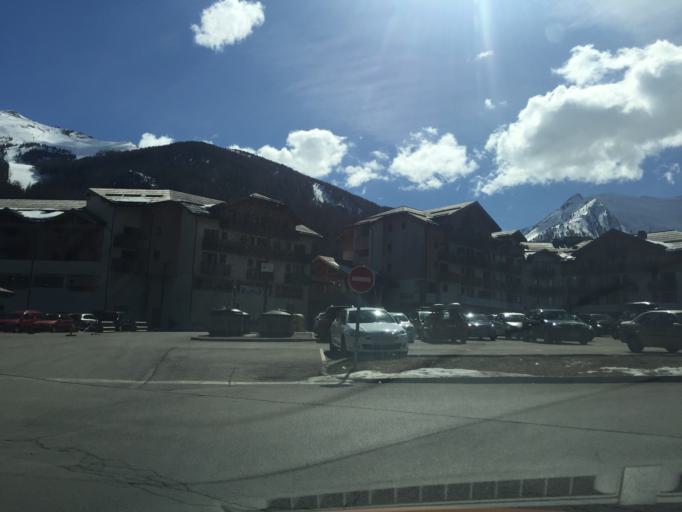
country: FR
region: Provence-Alpes-Cote d'Azur
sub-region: Departement des Hautes-Alpes
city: Embrun
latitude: 44.4860
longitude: 6.5531
